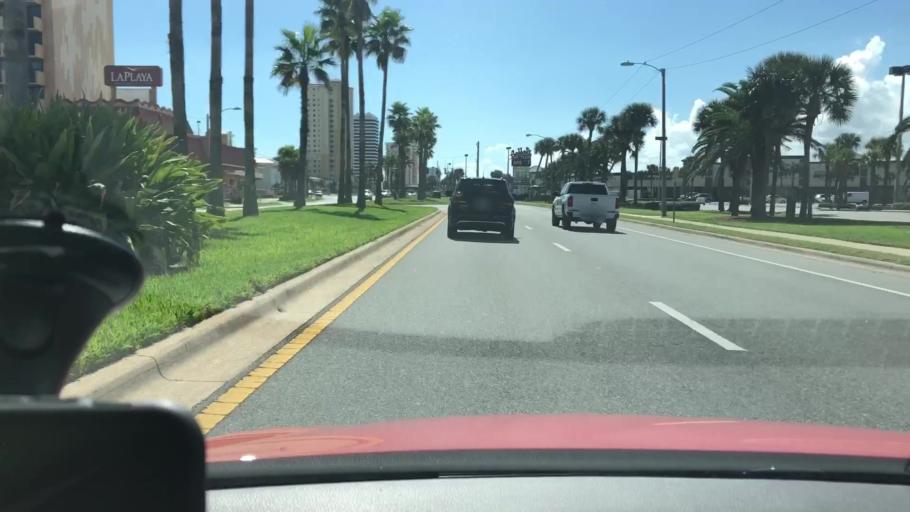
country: US
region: Florida
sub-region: Volusia County
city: Holly Hill
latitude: 29.2636
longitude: -81.0264
